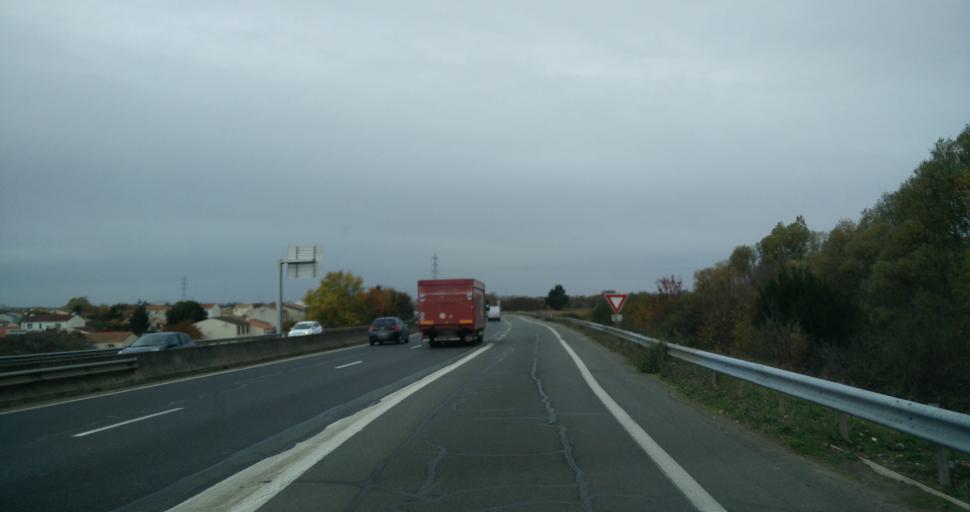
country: FR
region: Poitou-Charentes
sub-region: Departement de la Charente-Maritime
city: Puilboreau
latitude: 46.1783
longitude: -1.1281
